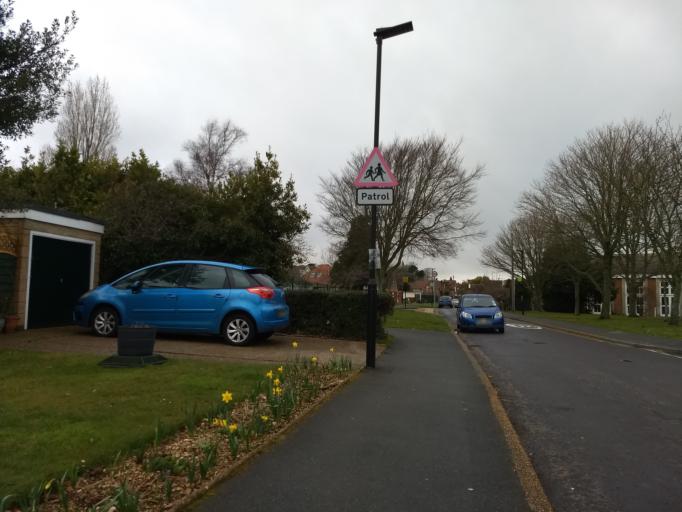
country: GB
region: England
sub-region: Isle of Wight
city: Bembridge
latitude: 50.6849
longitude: -1.0812
